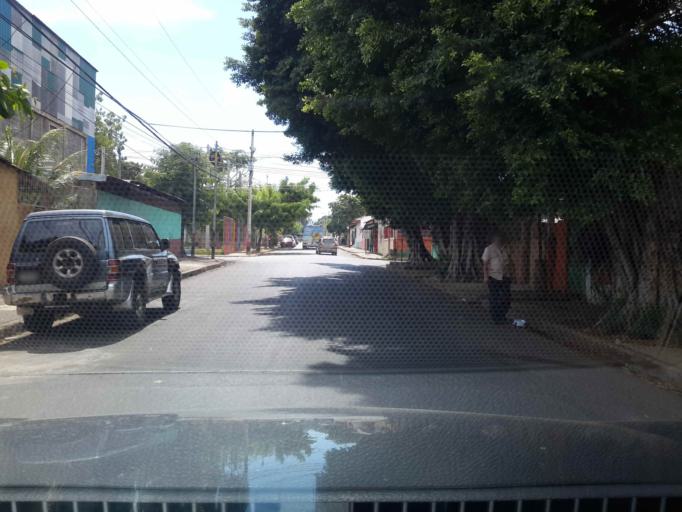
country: NI
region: Managua
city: Managua
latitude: 12.1334
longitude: -86.2948
